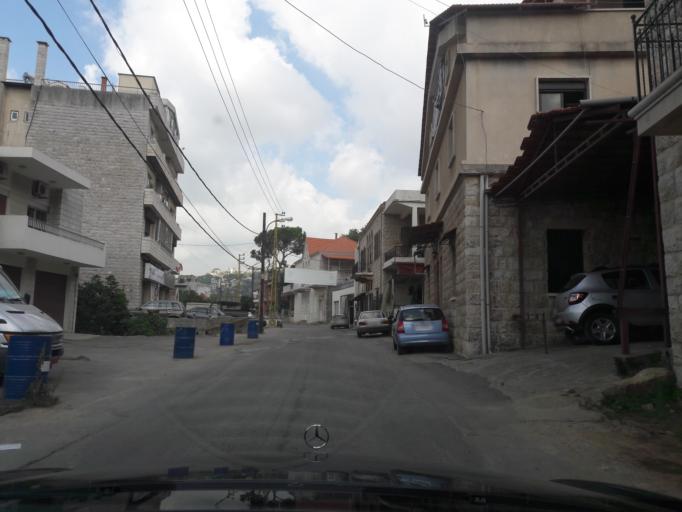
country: LB
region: Mont-Liban
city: Djounie
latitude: 33.9282
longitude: 35.6602
